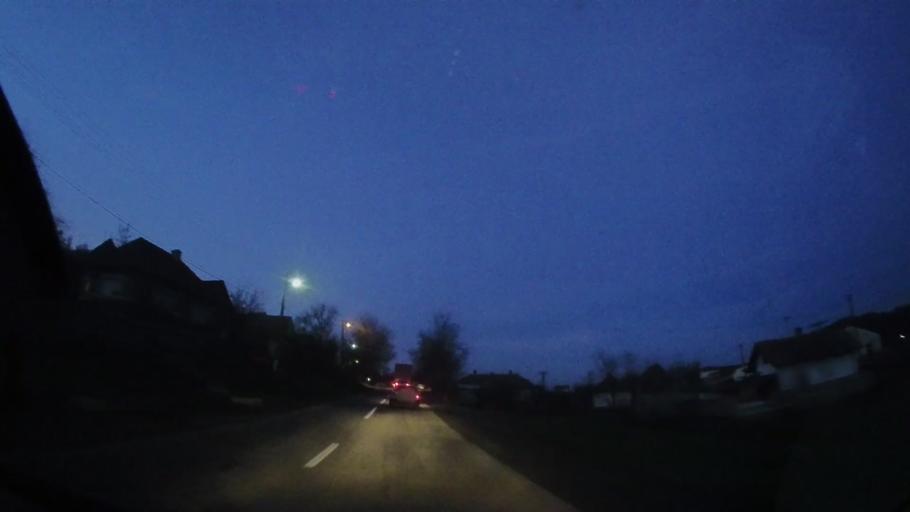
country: RO
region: Mures
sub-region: Comuna Sarmasu
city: Sarmasu
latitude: 46.7792
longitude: 24.2025
